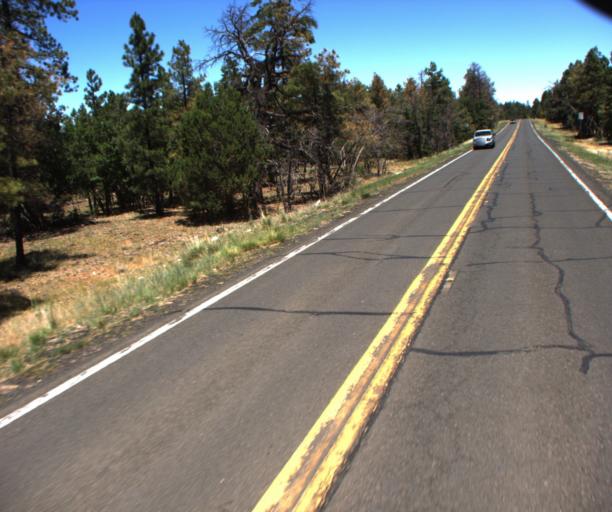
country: US
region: Arizona
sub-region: Gila County
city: Pine
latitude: 34.5885
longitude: -111.2537
